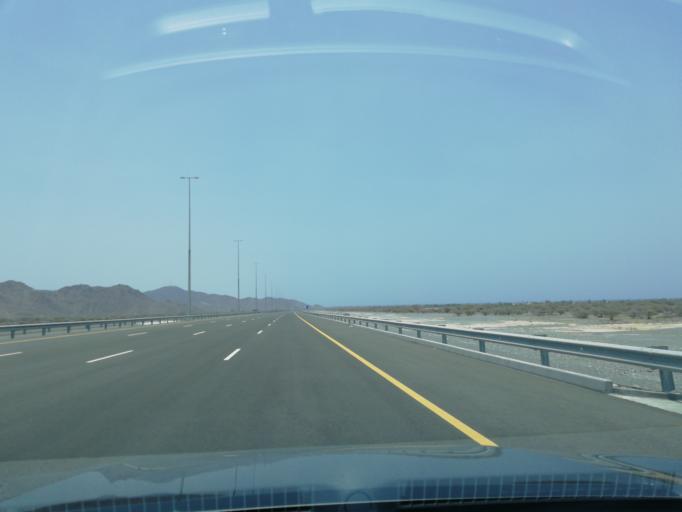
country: AE
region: Al Fujayrah
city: Al Fujayrah
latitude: 24.9302
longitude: 56.3563
